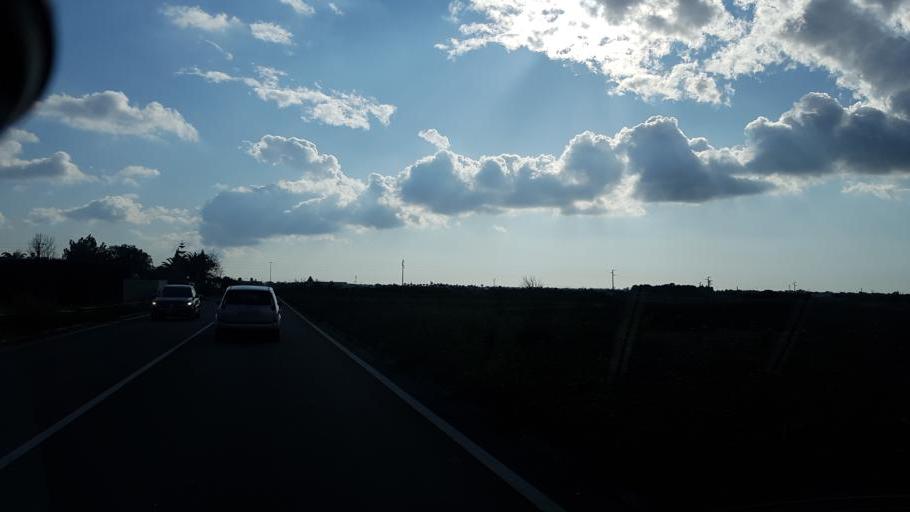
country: IT
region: Apulia
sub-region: Provincia di Lecce
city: Veglie
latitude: 40.3555
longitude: 17.9682
